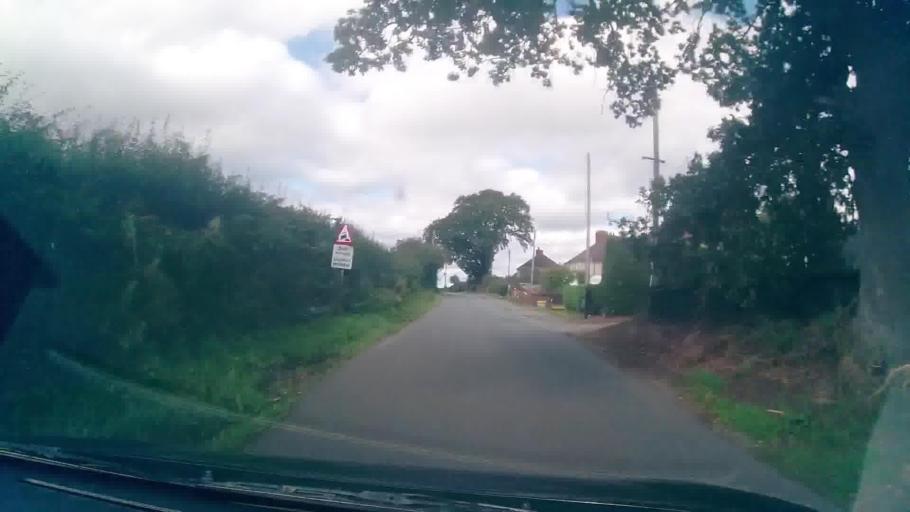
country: GB
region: England
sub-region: Shropshire
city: Whitchurch
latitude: 52.9451
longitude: -2.7313
